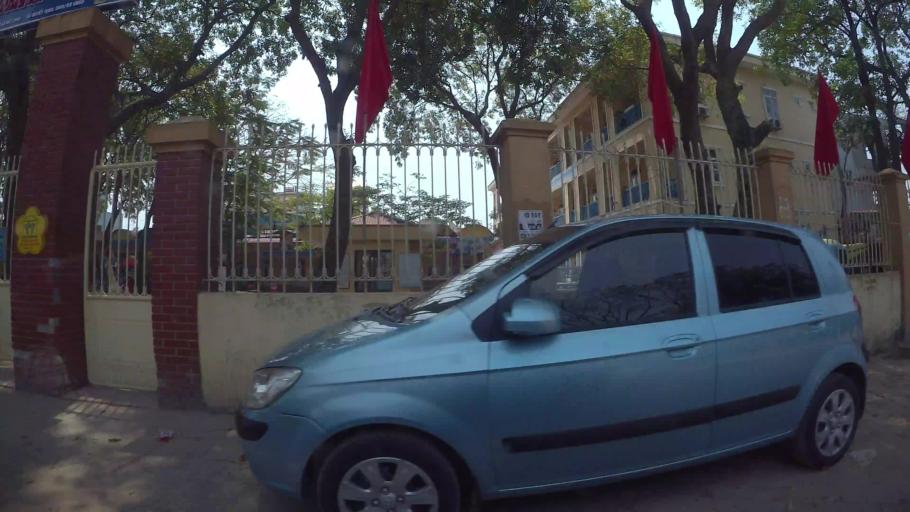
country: VN
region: Ha Noi
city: Van Dien
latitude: 20.9527
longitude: 105.8263
